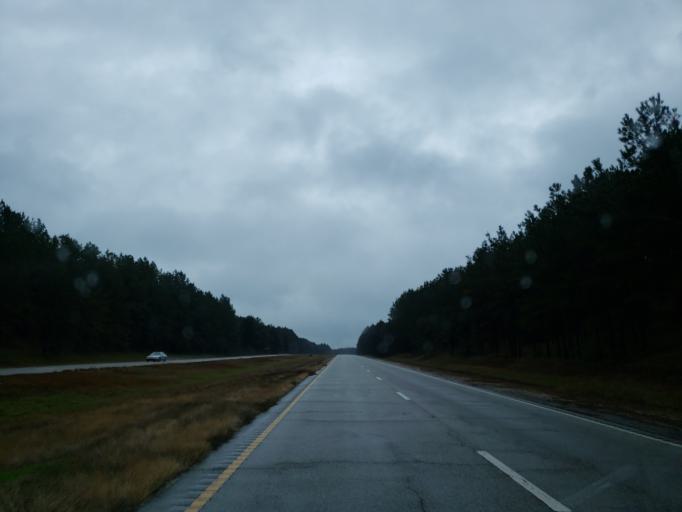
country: US
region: Mississippi
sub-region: Lauderdale County
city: Meridian
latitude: 32.2915
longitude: -88.6968
